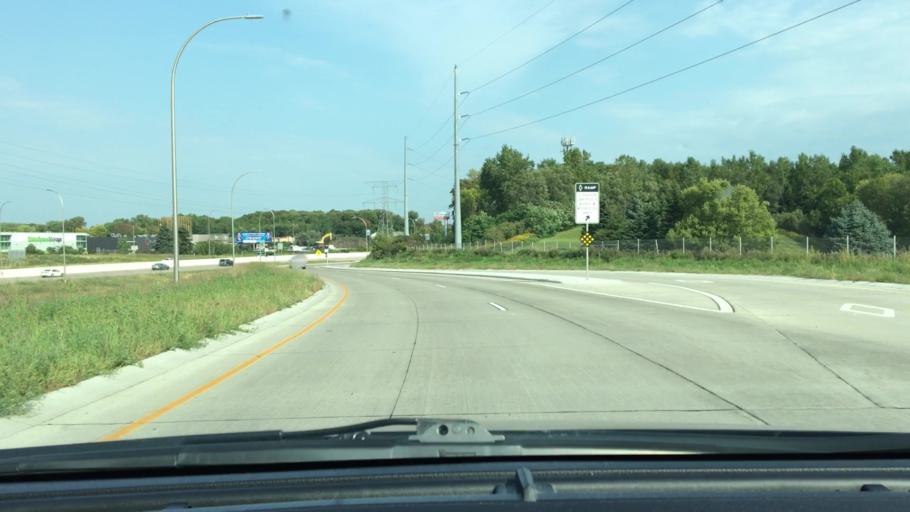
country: US
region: Minnesota
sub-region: Hennepin County
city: Plymouth
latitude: 45.0110
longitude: -93.4559
